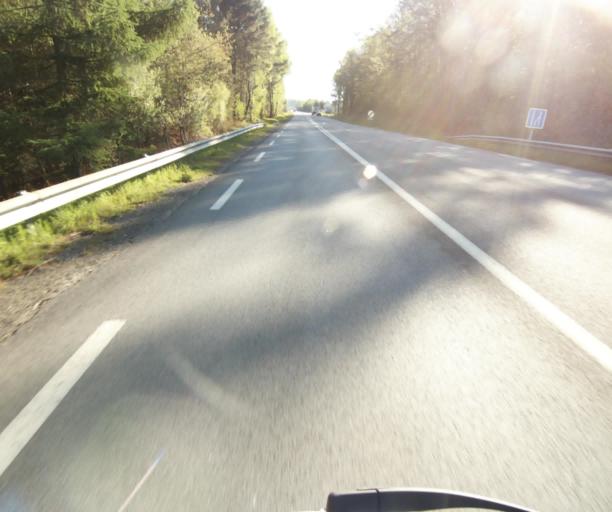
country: FR
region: Limousin
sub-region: Departement de la Correze
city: Correze
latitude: 45.3257
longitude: 1.8599
